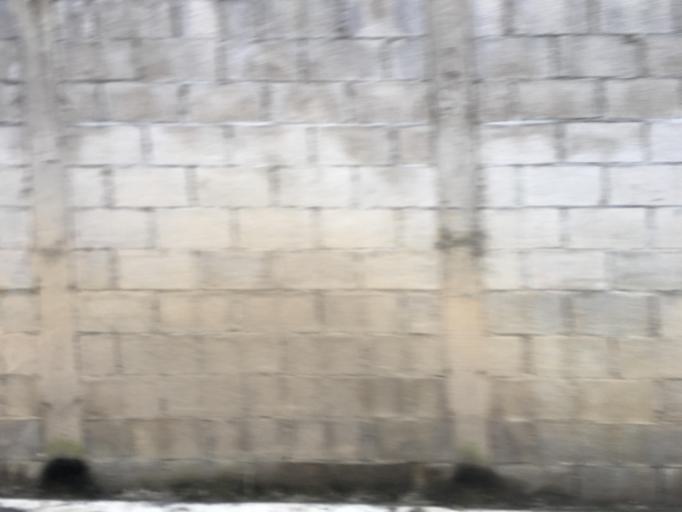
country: GT
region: Sacatepequez
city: Jocotenango
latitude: 14.5818
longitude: -90.7464
